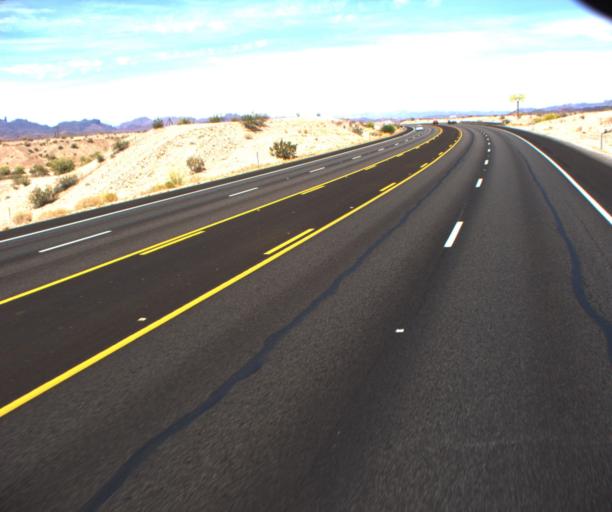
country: US
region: Arizona
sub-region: La Paz County
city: Cienega Springs
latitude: 34.1653
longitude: -114.2544
